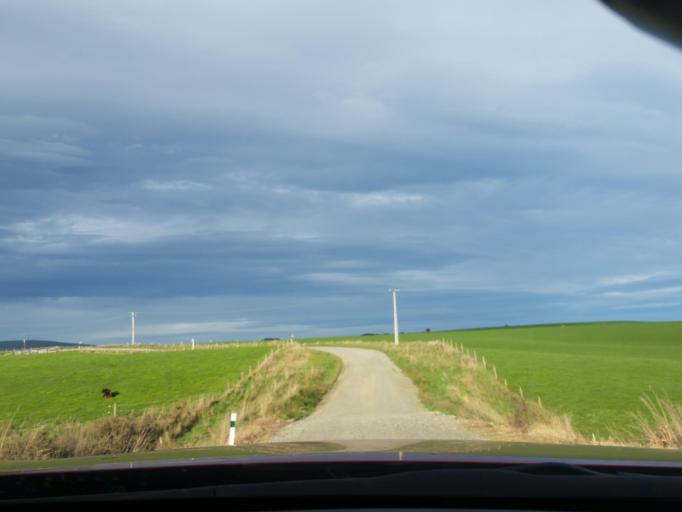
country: NZ
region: Southland
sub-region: Southland District
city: Riverton
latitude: -46.2970
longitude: 167.7391
